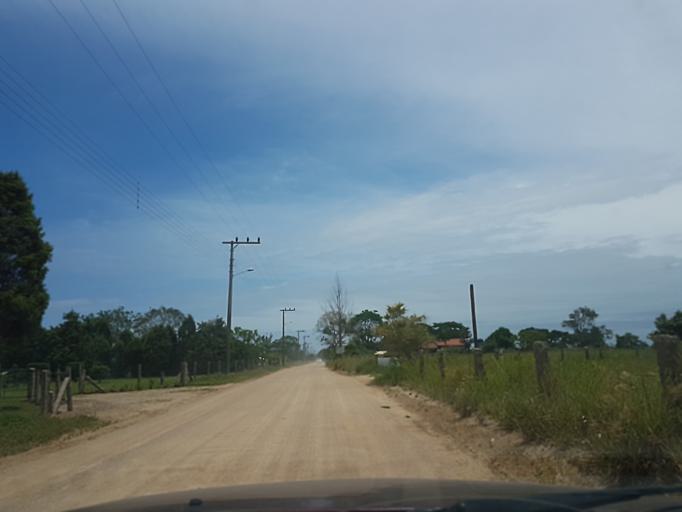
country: BR
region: Santa Catarina
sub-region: Jaguaruna
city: Jaguaruna
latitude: -28.6397
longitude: -48.9621
